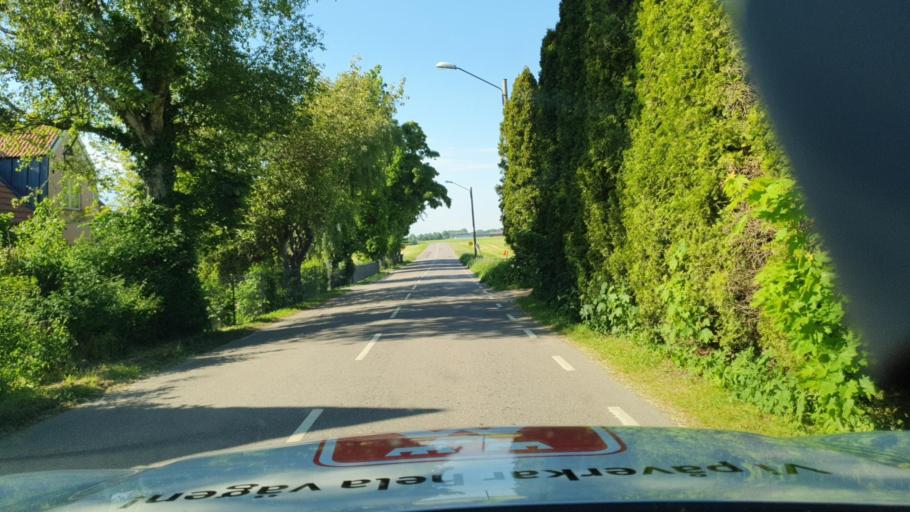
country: SE
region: Skane
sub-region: Ystads Kommun
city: Kopingebro
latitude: 55.4842
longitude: 13.9502
